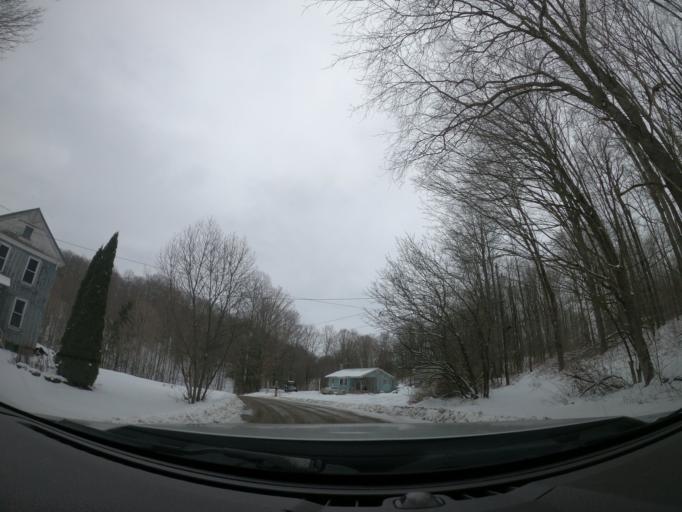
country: US
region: New York
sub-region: Cayuga County
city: Moravia
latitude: 42.7315
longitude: -76.2838
